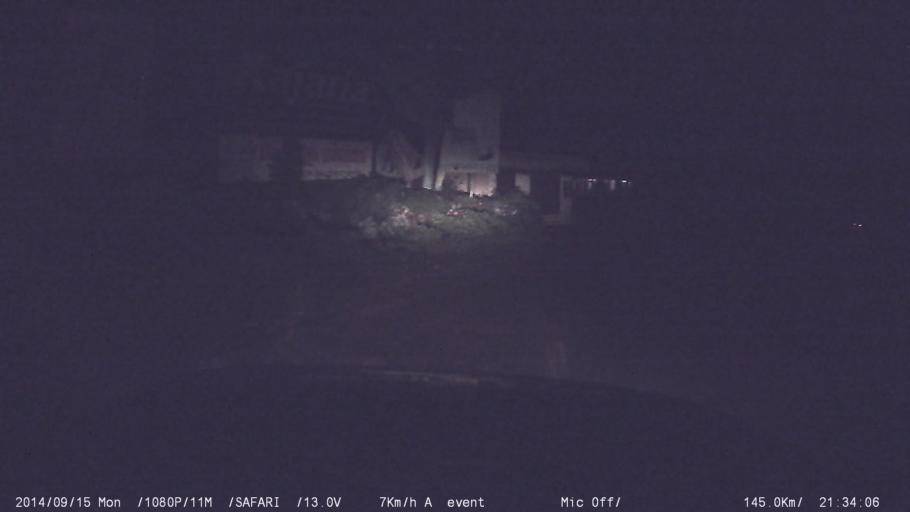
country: IN
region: Kerala
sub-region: Kottayam
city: Palackattumala
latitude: 9.7096
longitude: 76.5543
